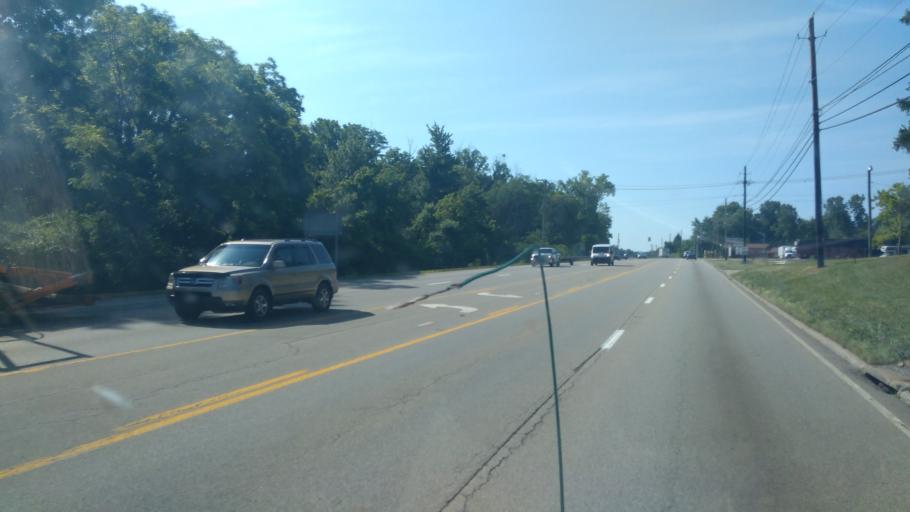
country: US
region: Ohio
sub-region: Delaware County
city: Delaware
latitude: 40.3205
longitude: -83.0701
